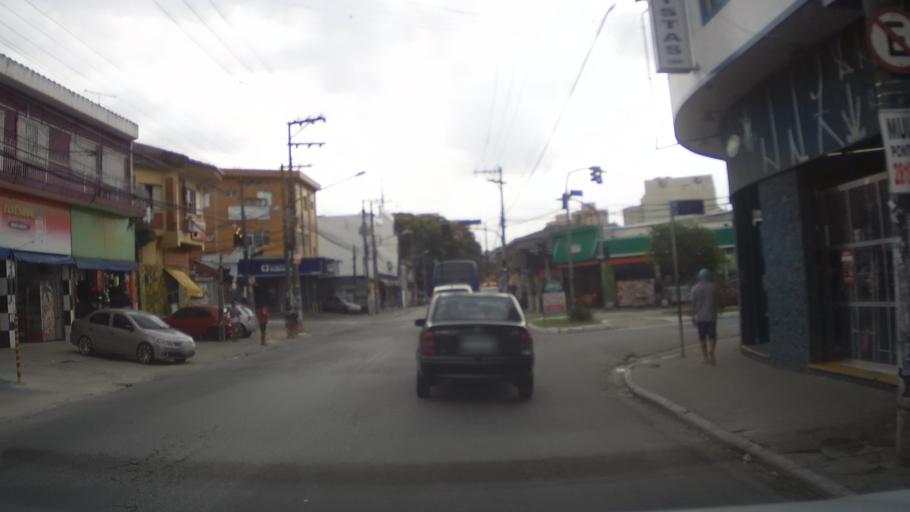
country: BR
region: Sao Paulo
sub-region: Guarulhos
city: Guarulhos
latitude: -23.4287
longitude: -46.5008
